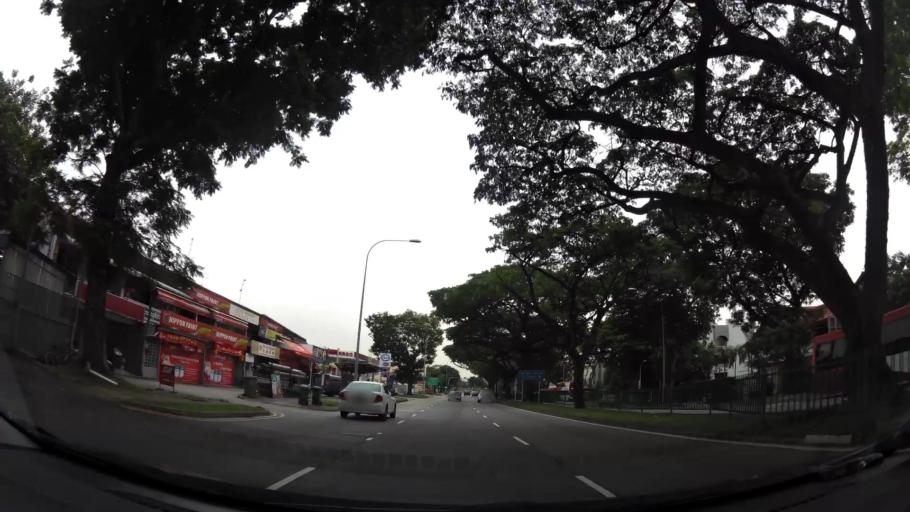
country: SG
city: Singapore
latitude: 1.3616
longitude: 103.8735
